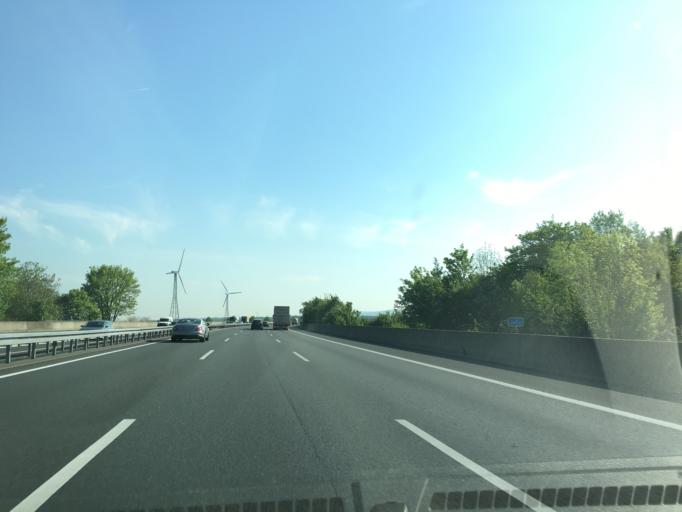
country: DE
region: Lower Saxony
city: Pohle
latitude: 52.2477
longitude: 9.2898
